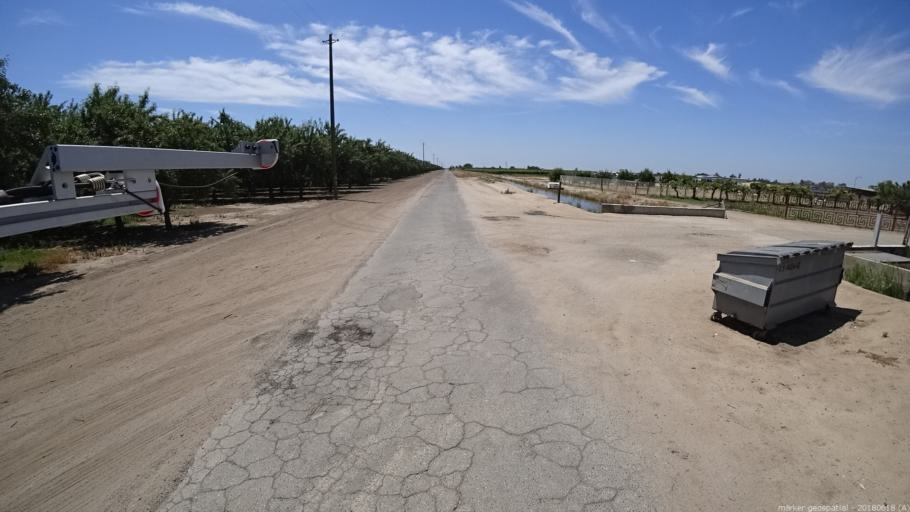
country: US
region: California
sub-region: Madera County
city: Parkwood
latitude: 36.8899
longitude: -120.1011
